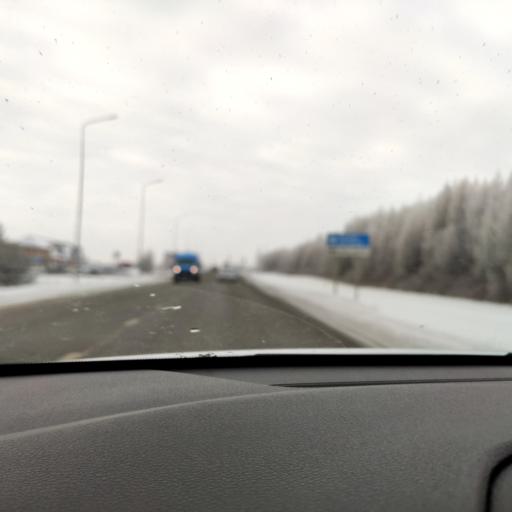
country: RU
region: Tatarstan
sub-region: Arskiy Rayon
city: Arsk
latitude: 56.1057
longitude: 49.8849
